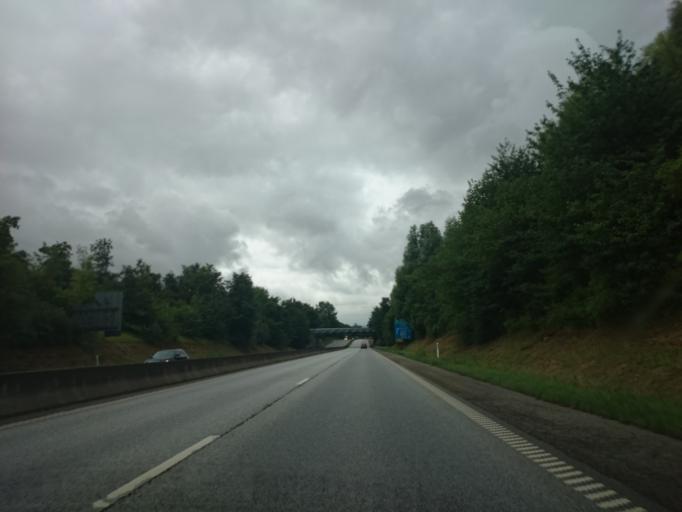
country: SE
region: Skane
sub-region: Lunds Kommun
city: Lund
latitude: 55.7055
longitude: 13.2200
